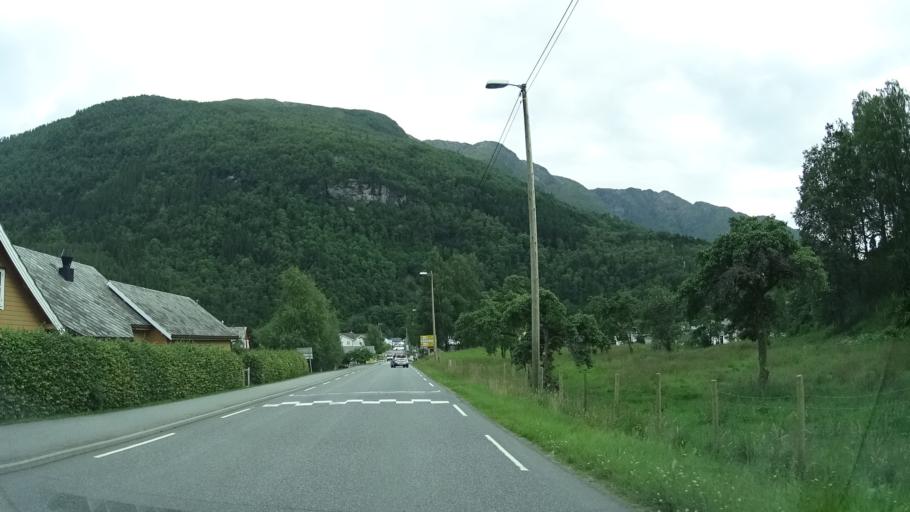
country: NO
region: Hordaland
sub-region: Jondal
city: Jondal
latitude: 60.2787
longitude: 6.2510
